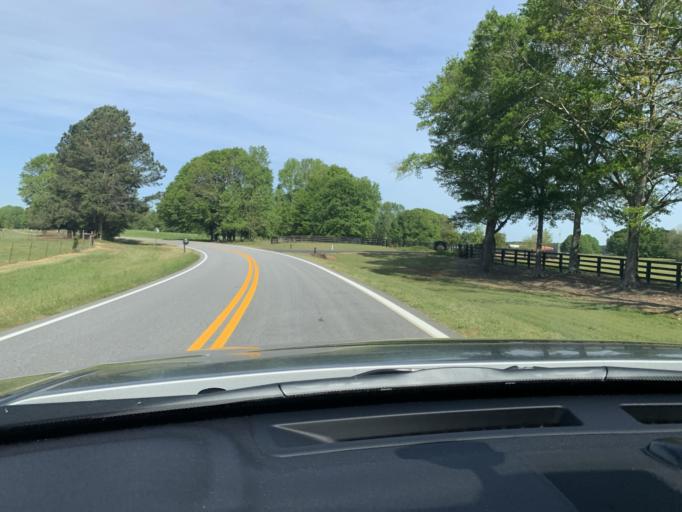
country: US
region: Georgia
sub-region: Oconee County
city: Watkinsville
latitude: 33.8135
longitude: -83.4066
